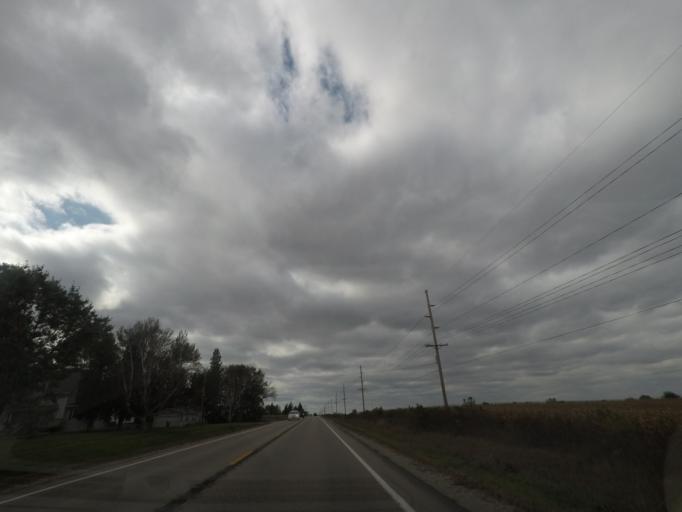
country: US
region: Iowa
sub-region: Story County
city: Huxley
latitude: 41.8778
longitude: -93.5493
